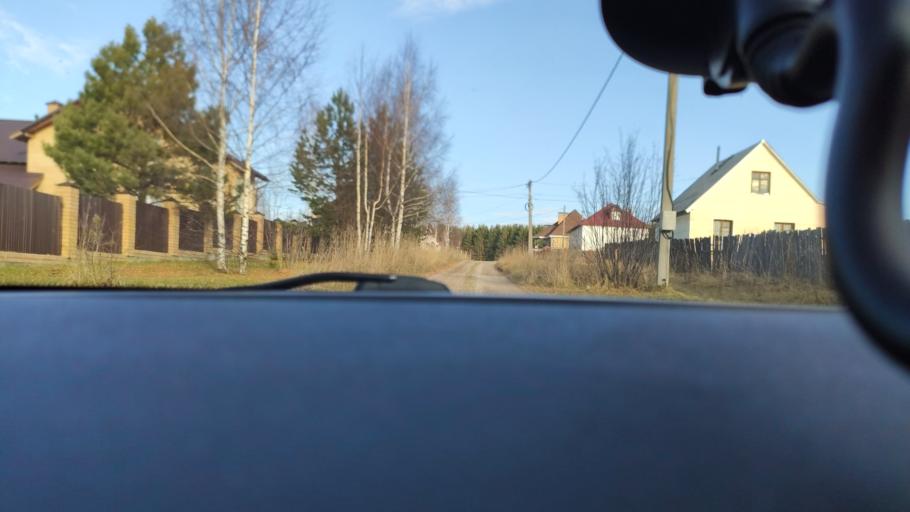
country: RU
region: Perm
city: Kondratovo
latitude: 58.0605
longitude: 56.0362
